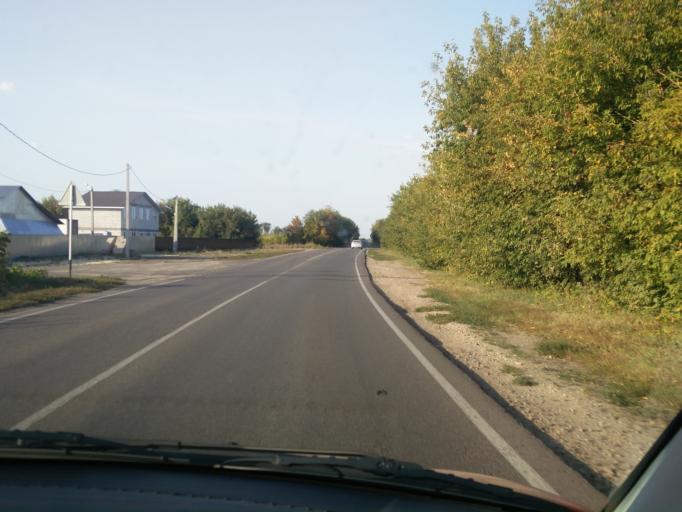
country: RU
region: Voronezj
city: Ramon'
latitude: 51.9190
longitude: 39.3208
